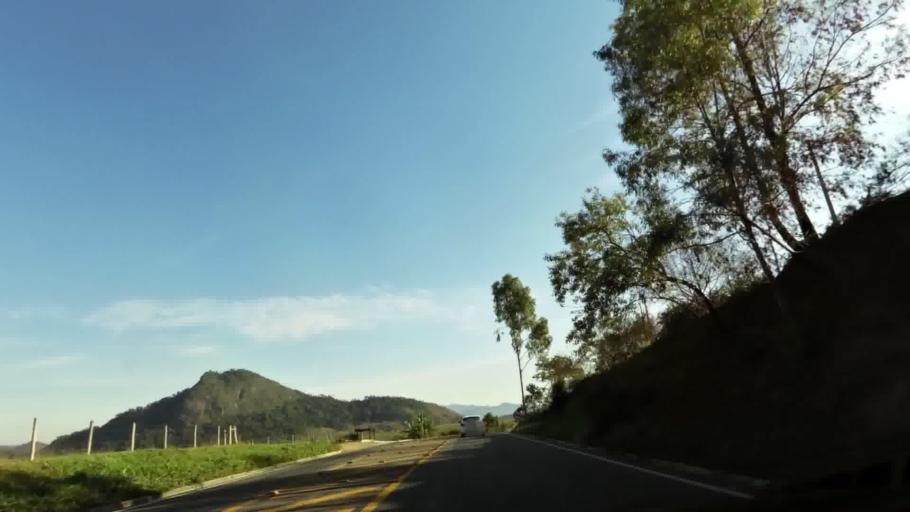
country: BR
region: Espirito Santo
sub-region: Viana
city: Viana
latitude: -20.4929
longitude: -40.4770
